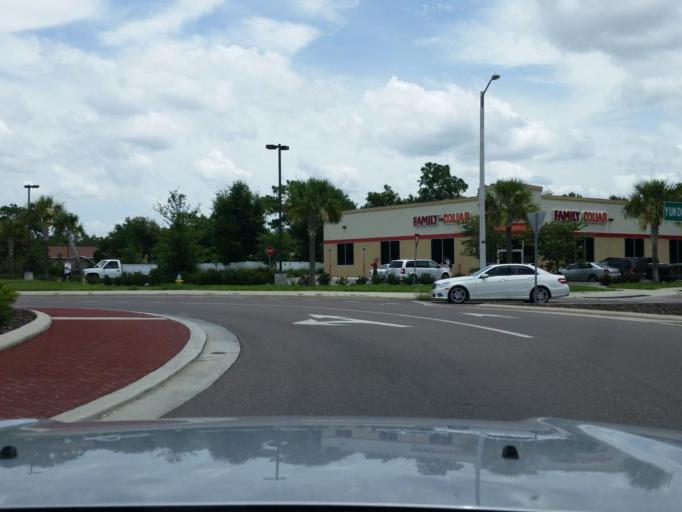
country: US
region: Florida
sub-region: Hillsborough County
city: Temple Terrace
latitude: 28.0289
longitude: -82.4162
